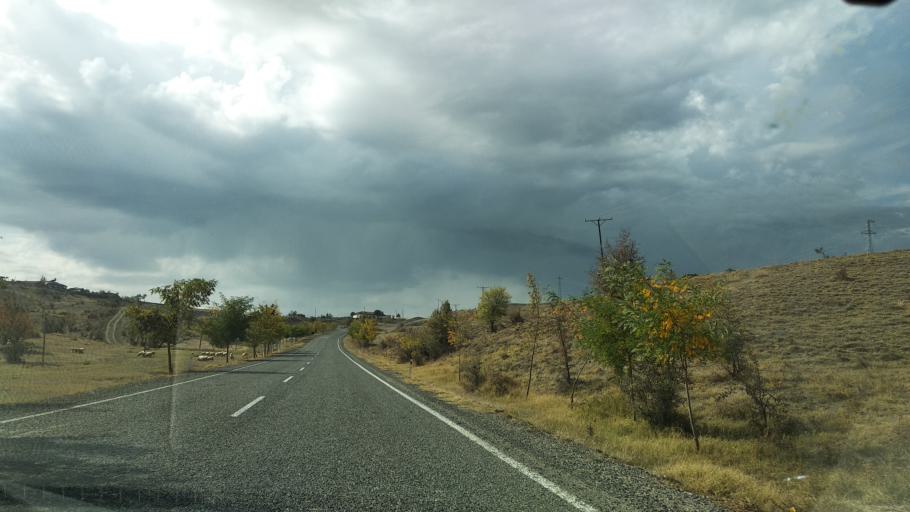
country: TR
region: Bolu
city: Seben
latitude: 40.3806
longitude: 31.5242
